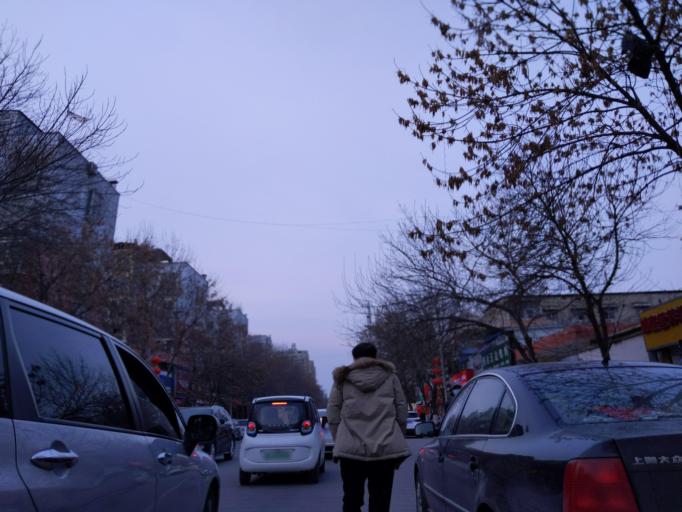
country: CN
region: Henan Sheng
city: Zhongyuanlu
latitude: 35.7827
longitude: 115.0390
